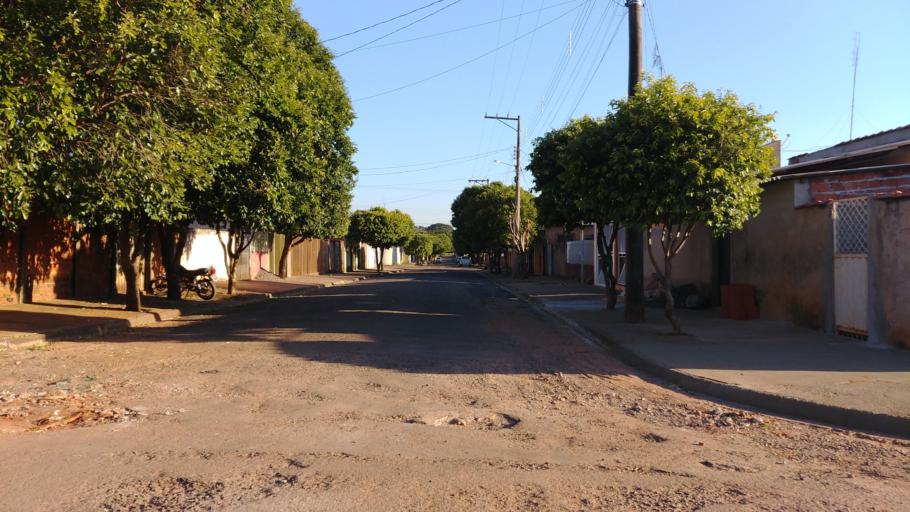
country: BR
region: Sao Paulo
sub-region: Paraguacu Paulista
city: Paraguacu Paulista
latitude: -22.4218
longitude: -50.5883
